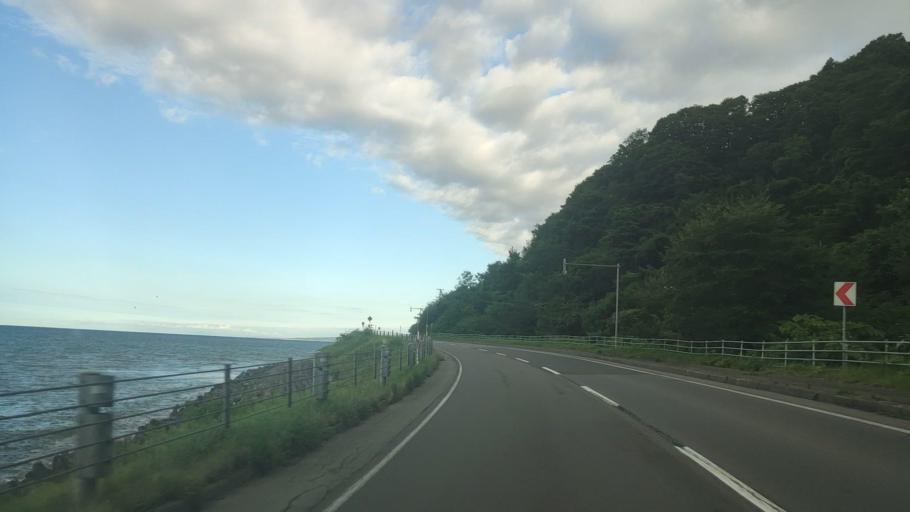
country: JP
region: Hokkaido
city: Nanae
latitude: 42.1518
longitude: 140.4889
